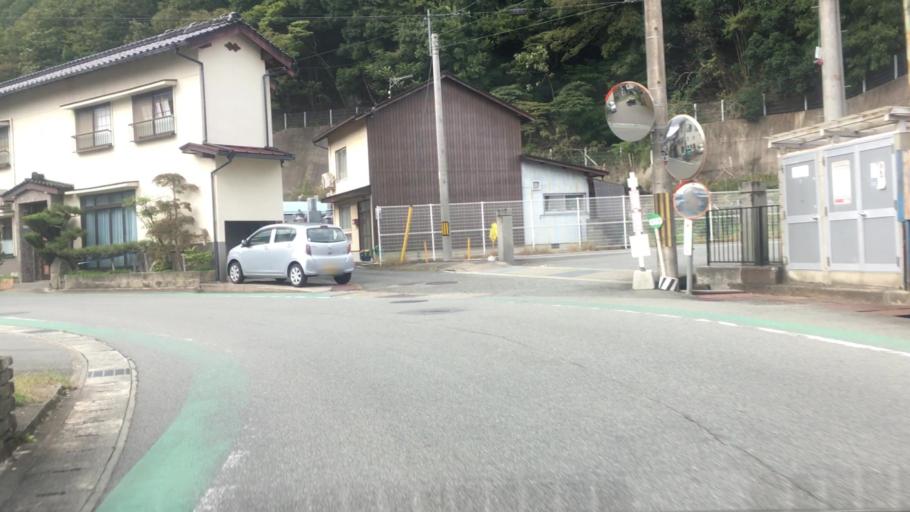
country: JP
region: Hyogo
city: Toyooka
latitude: 35.4069
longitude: 134.7637
